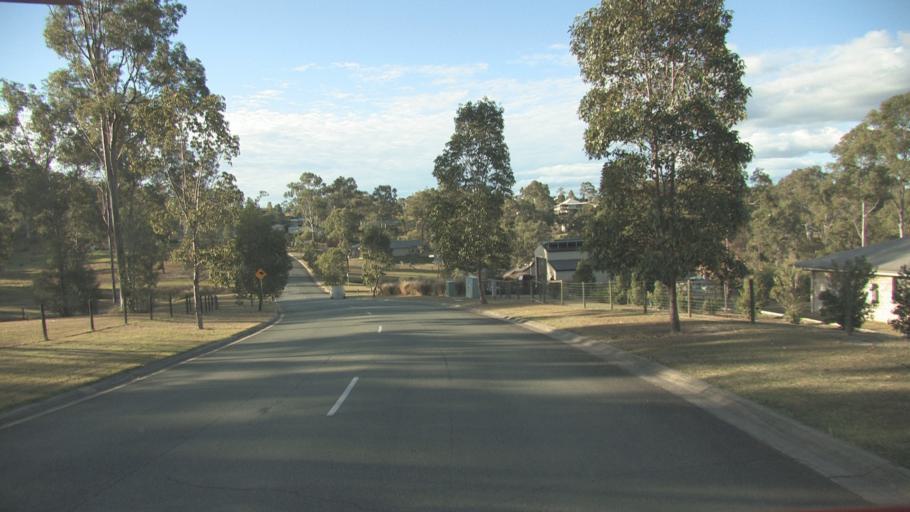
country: AU
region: Queensland
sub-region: Logan
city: Cedar Vale
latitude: -27.8729
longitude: 153.0761
